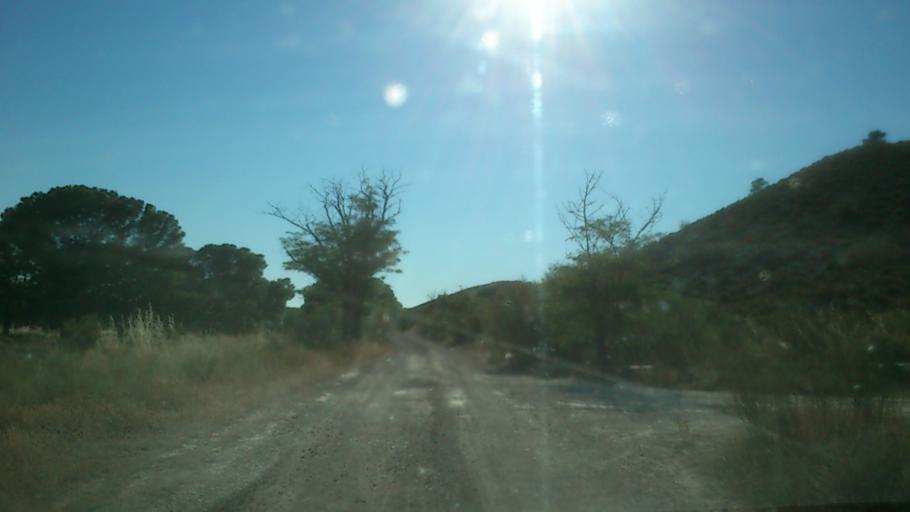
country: ES
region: Aragon
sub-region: Provincia de Zaragoza
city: San Mateo de Gallego
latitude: 41.7681
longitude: -0.7519
